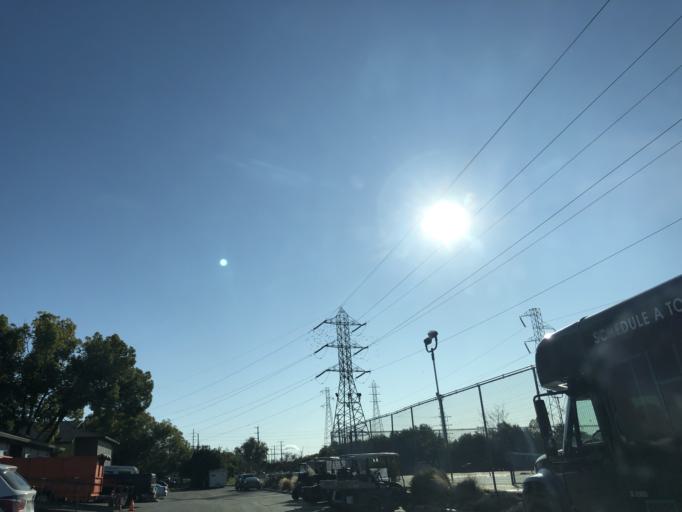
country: US
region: California
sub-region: Sacramento County
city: Rosemont
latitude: 38.5522
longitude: -121.4079
